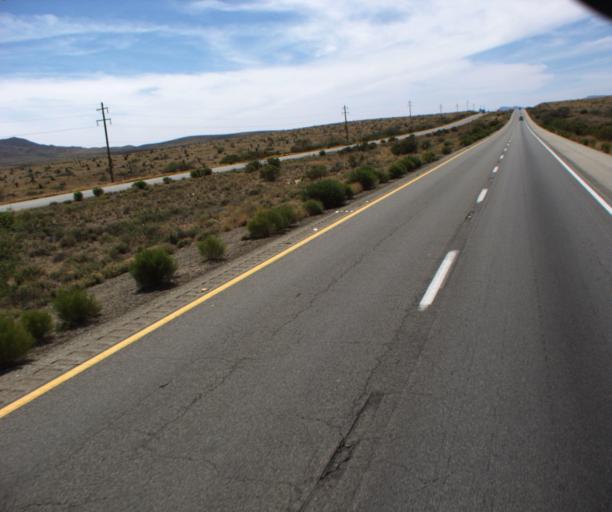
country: US
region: Arizona
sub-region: Cochise County
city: Willcox
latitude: 32.3542
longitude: -109.7121
